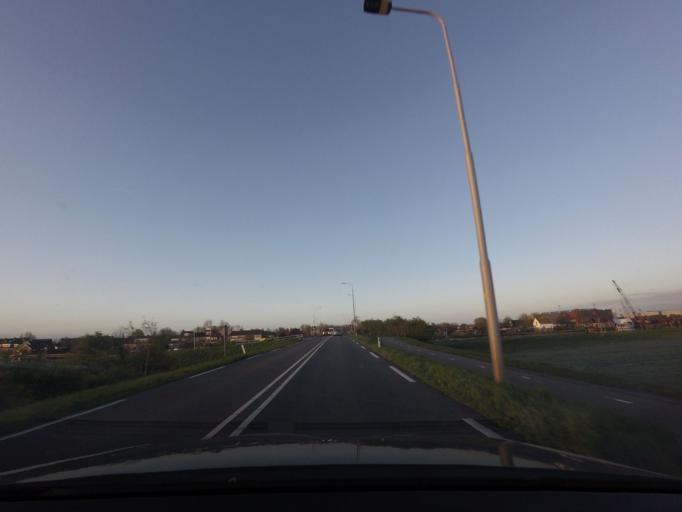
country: NL
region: North Holland
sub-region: Gemeente Zaanstad
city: Zaanstad
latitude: 52.5204
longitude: 4.7849
